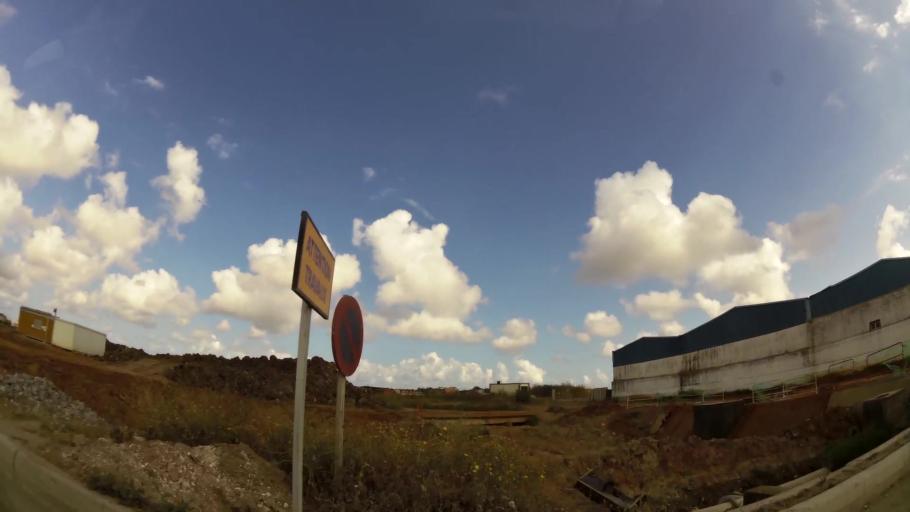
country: MA
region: Gharb-Chrarda-Beni Hssen
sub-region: Kenitra Province
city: Kenitra
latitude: 34.2726
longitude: -6.5645
